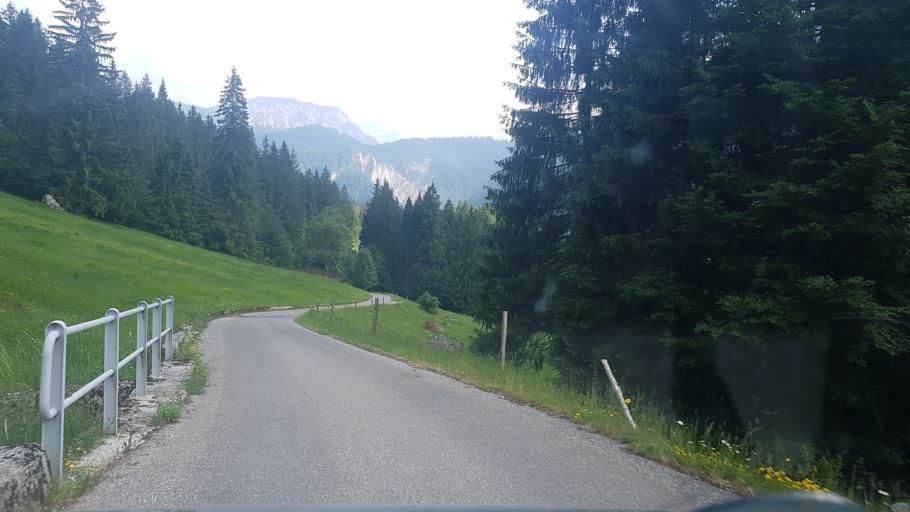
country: IT
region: Friuli Venezia Giulia
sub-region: Provincia di Udine
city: Paularo
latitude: 46.5436
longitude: 13.2041
